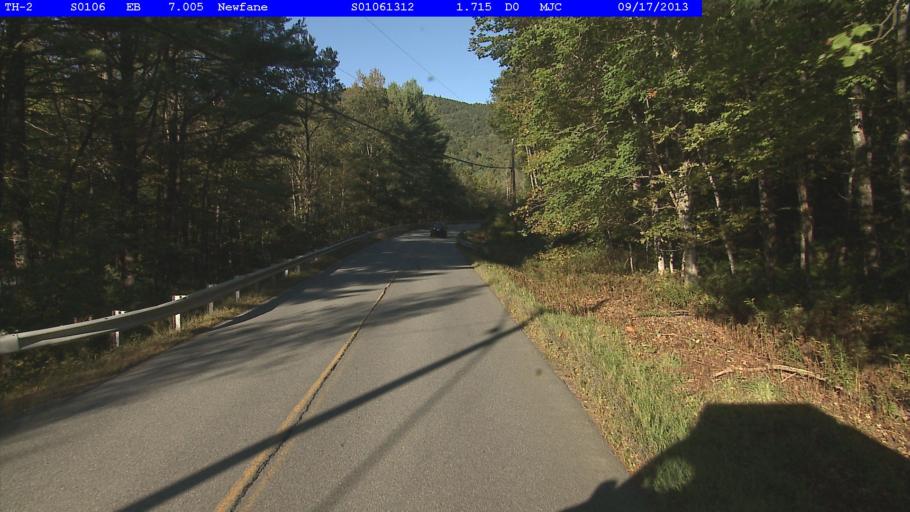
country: US
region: Vermont
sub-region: Windham County
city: Dover
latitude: 42.9450
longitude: -72.7364
